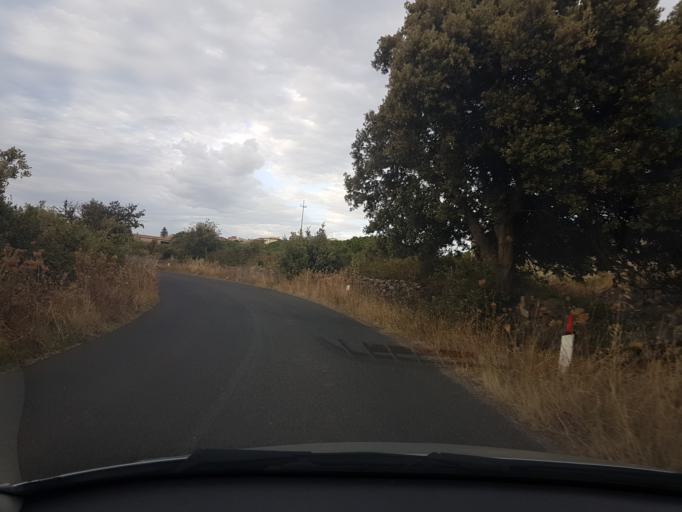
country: IT
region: Sardinia
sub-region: Provincia di Oristano
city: Seneghe
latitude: 40.0770
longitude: 8.6066
